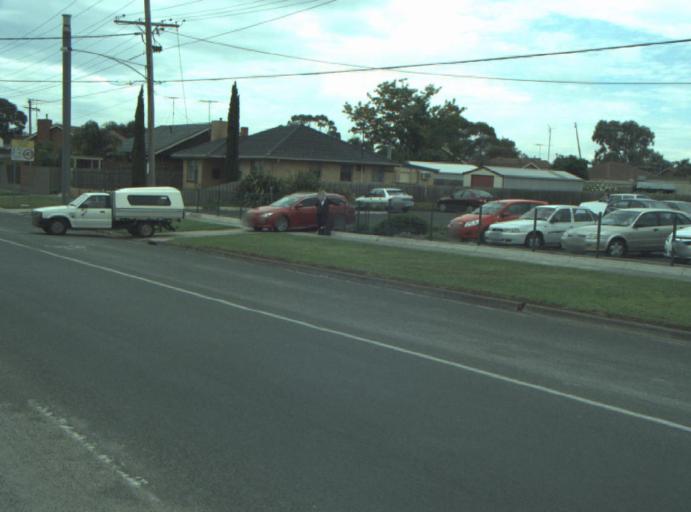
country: AU
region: Victoria
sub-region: Greater Geelong
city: Breakwater
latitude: -38.1718
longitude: 144.3840
